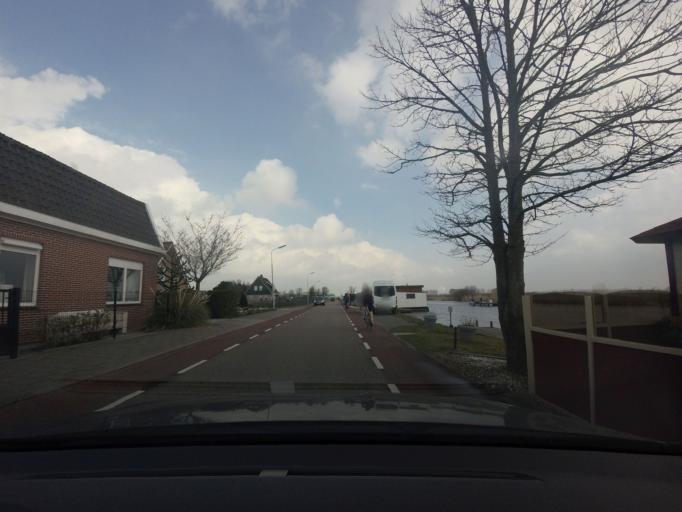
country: NL
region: North Holland
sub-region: Gemeente Haarlemmermeer
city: Hoofddorp
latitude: 52.3602
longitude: 4.7551
